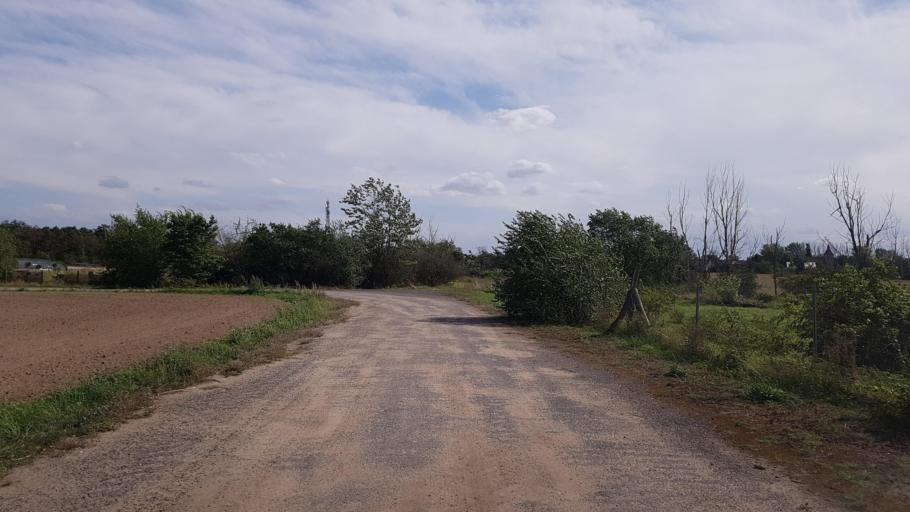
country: DE
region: Brandenburg
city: Muhlberg
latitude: 51.4281
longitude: 13.2629
